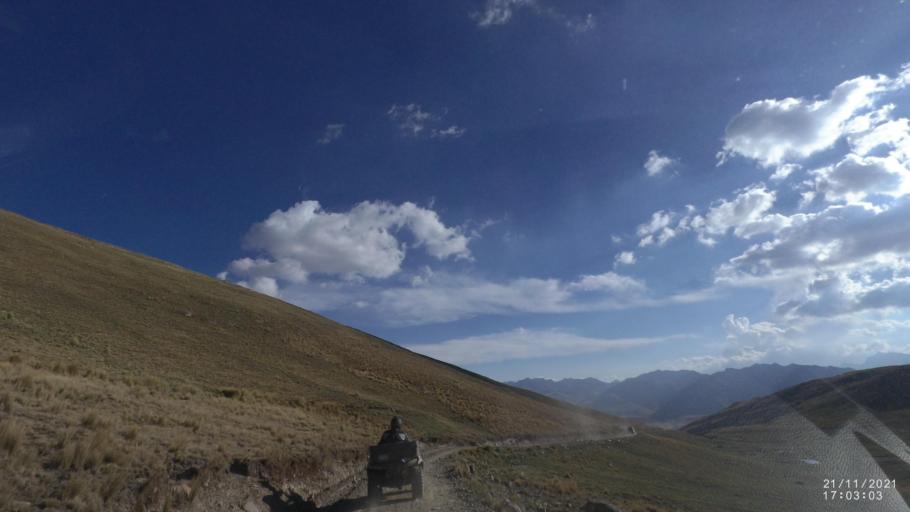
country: BO
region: Cochabamba
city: Cochabamba
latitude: -17.1180
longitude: -66.2557
